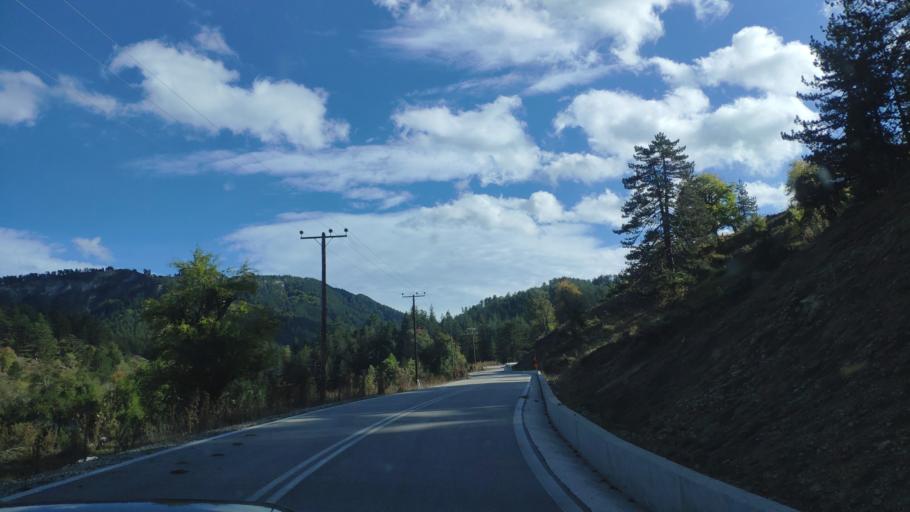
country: AL
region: Korce
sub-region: Rrethi i Devollit
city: Miras
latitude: 40.4016
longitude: 20.8821
